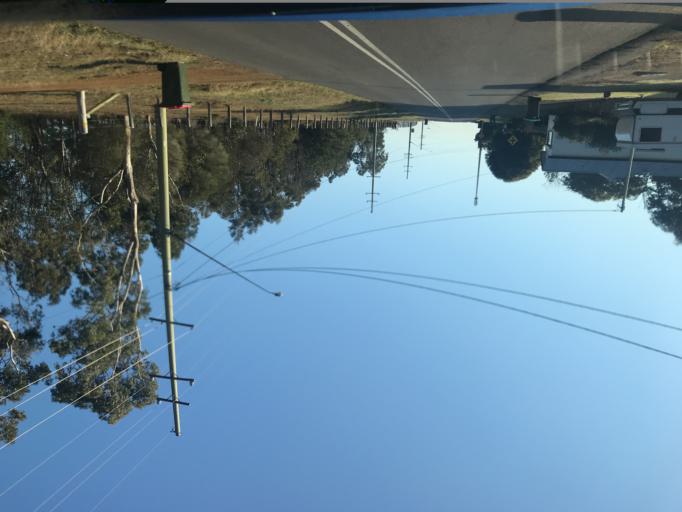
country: AU
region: New South Wales
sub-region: Cessnock
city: Cessnock
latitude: -32.9052
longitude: 151.2833
